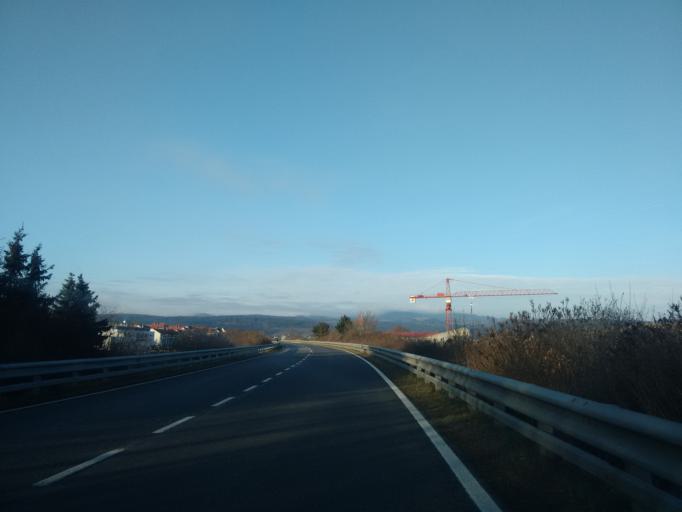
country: AT
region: Lower Austria
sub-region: Politischer Bezirk Melk
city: Melk
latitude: 48.2261
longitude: 15.3502
